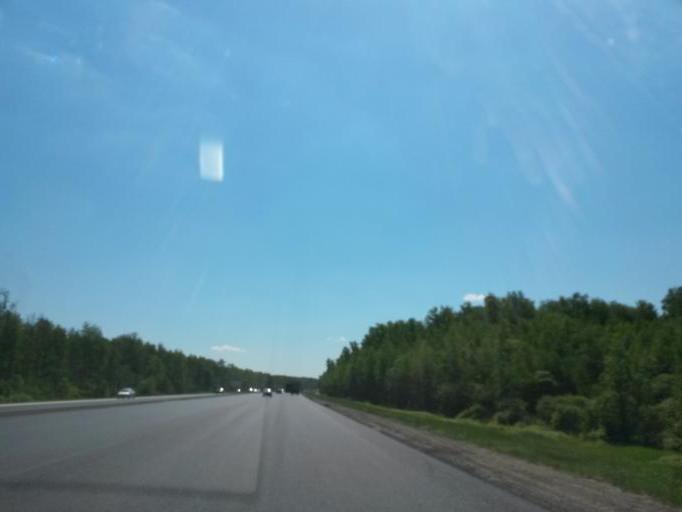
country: RU
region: Moskovskaya
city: Novyy Byt
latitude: 55.1139
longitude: 37.5782
